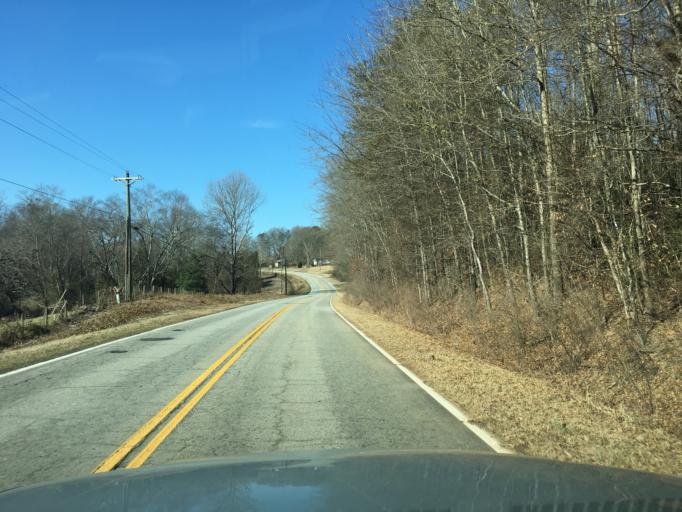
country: US
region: South Carolina
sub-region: Pickens County
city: Pickens
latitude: 34.8757
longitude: -82.6885
